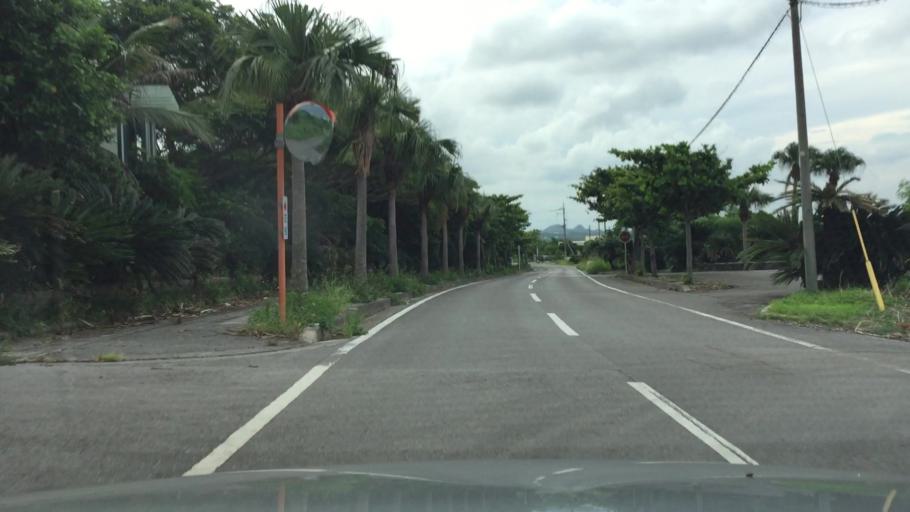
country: JP
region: Okinawa
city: Ishigaki
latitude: 24.4467
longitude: 124.1710
